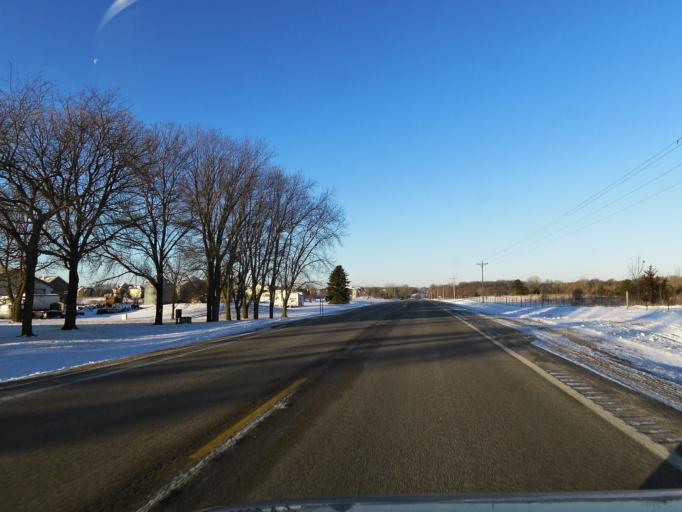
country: US
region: Minnesota
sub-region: Scott County
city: Prior Lake
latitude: 44.6743
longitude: -93.3888
